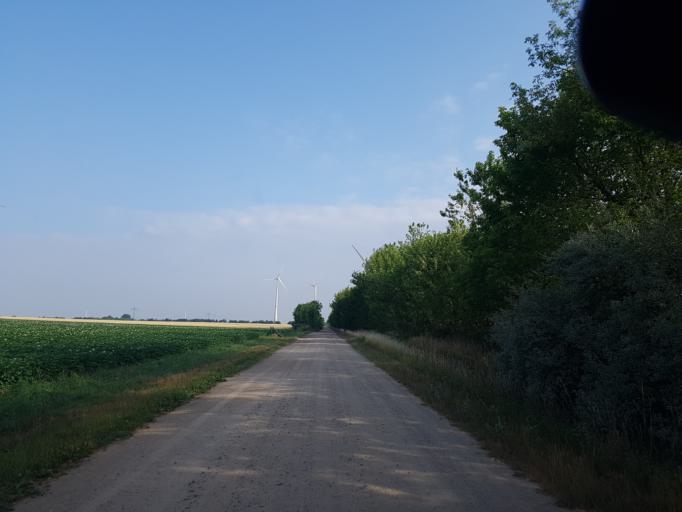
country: DE
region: Saxony-Anhalt
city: Kropstadt
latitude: 51.9887
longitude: 12.8198
